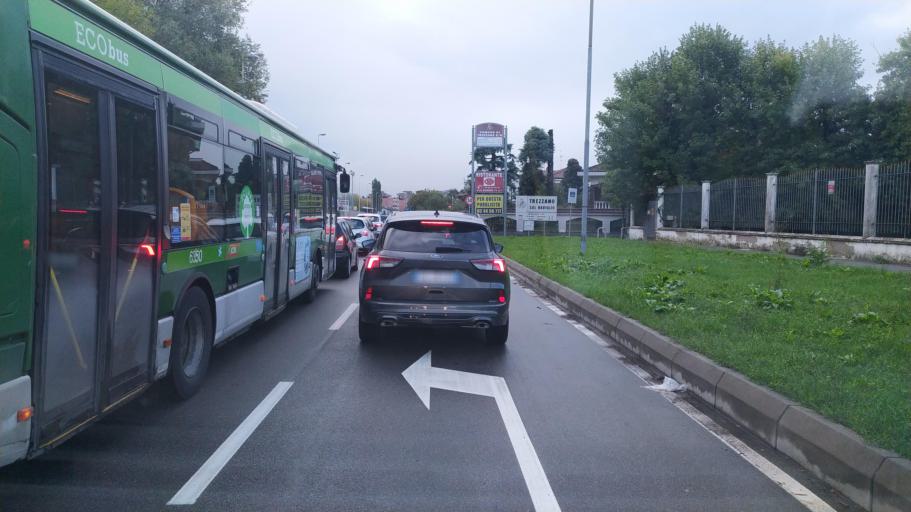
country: IT
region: Lombardy
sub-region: Citta metropolitana di Milano
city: Trezzano sul Naviglio
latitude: 45.4317
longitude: 9.0511
